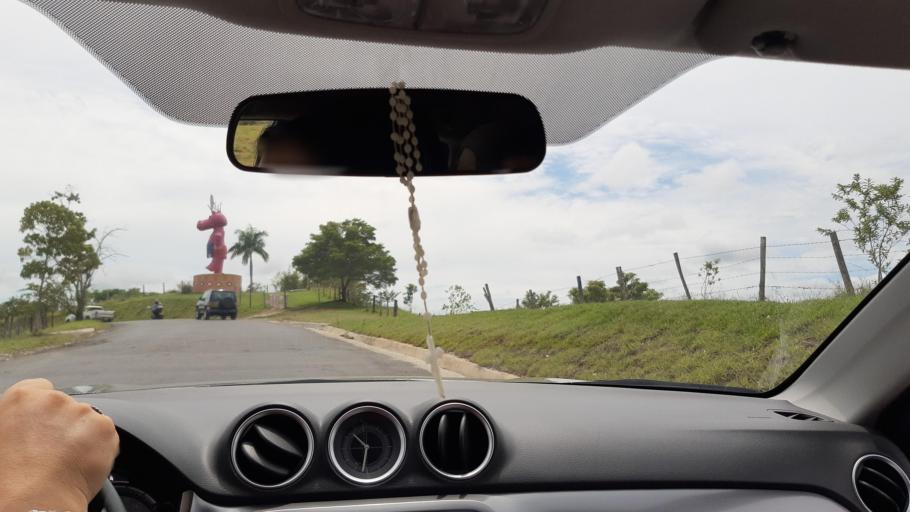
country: CO
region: Antioquia
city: Puerto Triunfo
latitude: 5.9045
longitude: -74.7192
